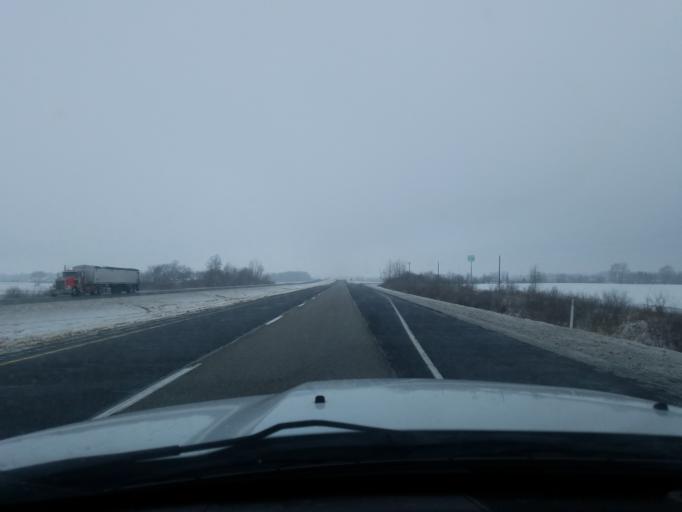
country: US
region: Indiana
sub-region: Fulton County
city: Rochester
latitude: 41.0440
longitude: -86.2106
